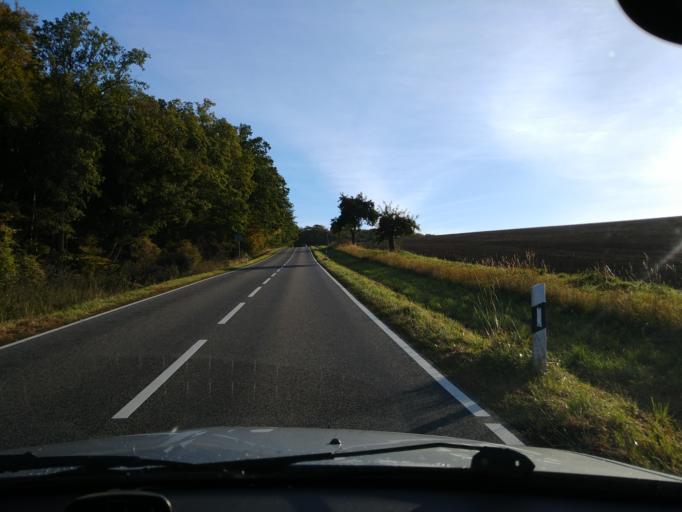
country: DE
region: Hesse
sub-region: Regierungsbezirk Darmstadt
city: Waldems
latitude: 50.2587
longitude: 8.3178
